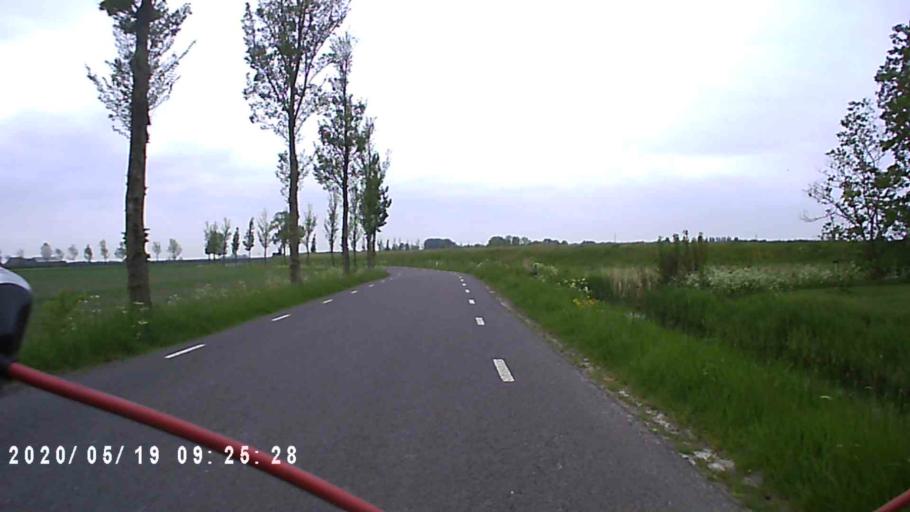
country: NL
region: Groningen
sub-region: Gemeente Zuidhorn
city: Grijpskerk
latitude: 53.2914
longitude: 6.3345
